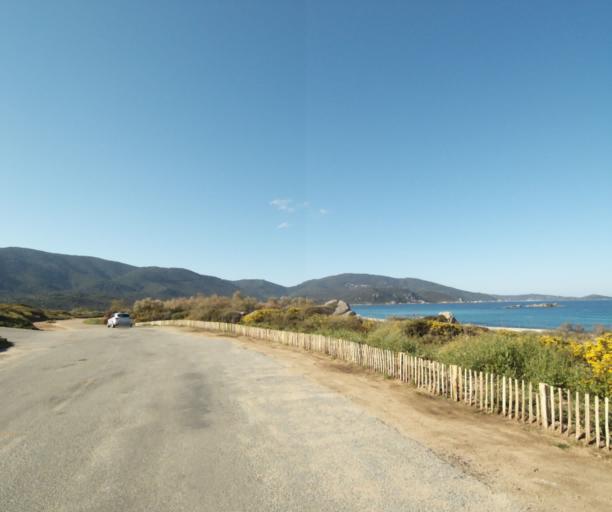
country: FR
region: Corsica
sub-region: Departement de la Corse-du-Sud
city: Propriano
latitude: 41.6662
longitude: 8.8824
